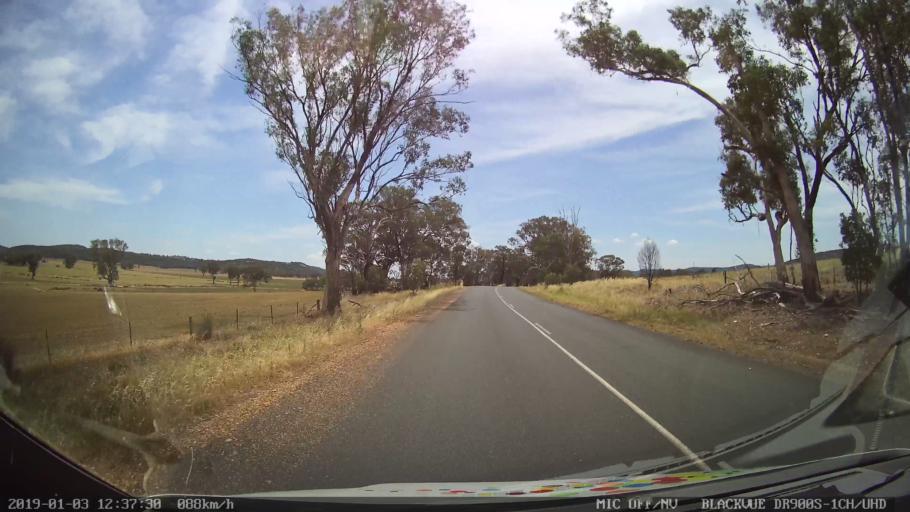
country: AU
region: New South Wales
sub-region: Weddin
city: Grenfell
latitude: -33.8419
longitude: 148.1850
